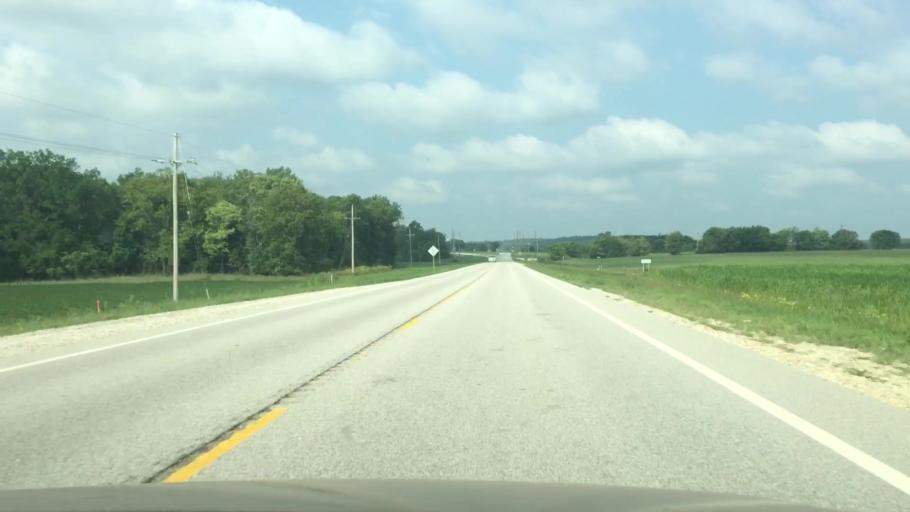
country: US
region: Kansas
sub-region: Anderson County
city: Garnett
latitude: 38.3627
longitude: -95.1326
